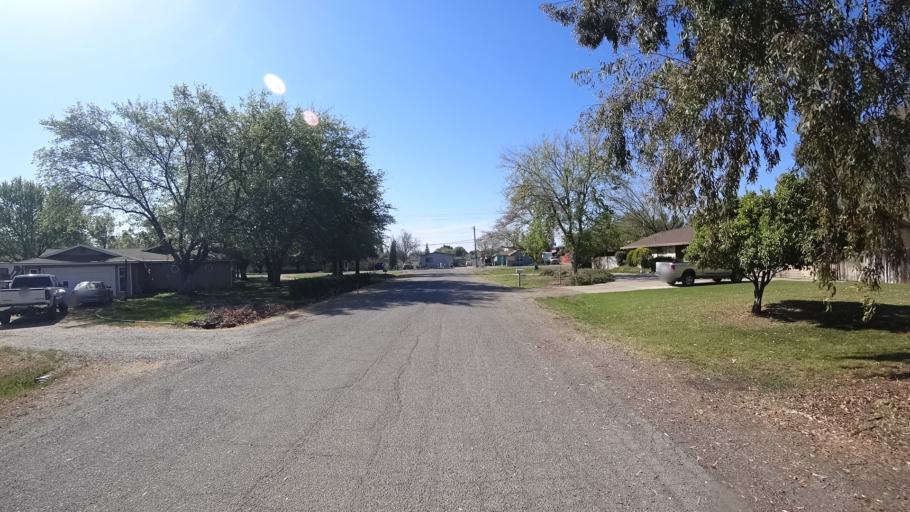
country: US
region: California
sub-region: Glenn County
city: Willows
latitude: 39.5340
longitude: -122.2043
